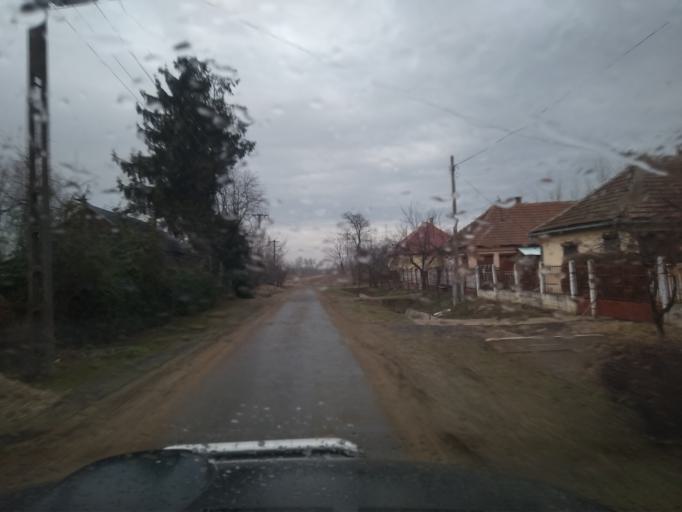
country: HU
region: Szabolcs-Szatmar-Bereg
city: Apagy
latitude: 47.9675
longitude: 21.9233
